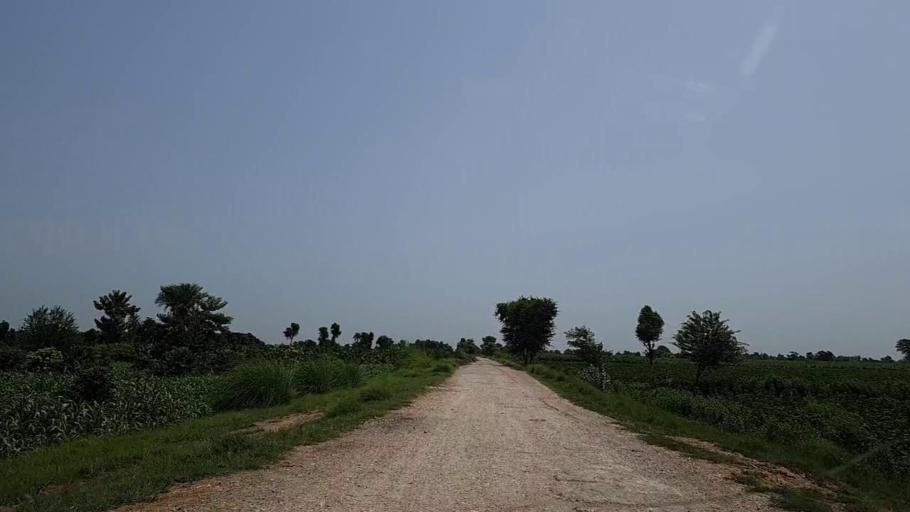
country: PK
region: Sindh
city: Naushahro Firoz
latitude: 26.8410
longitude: 67.9680
